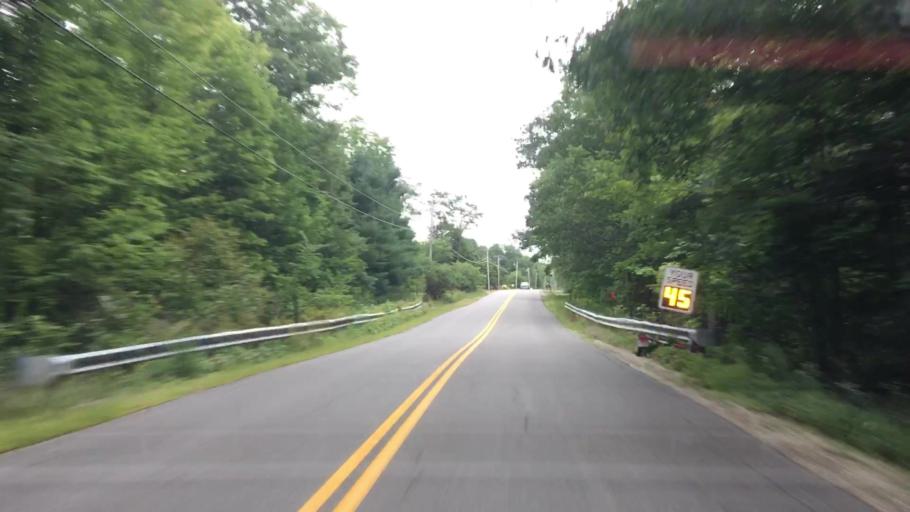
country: US
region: Maine
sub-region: Cumberland County
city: Yarmouth
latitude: 43.8984
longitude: -70.1974
